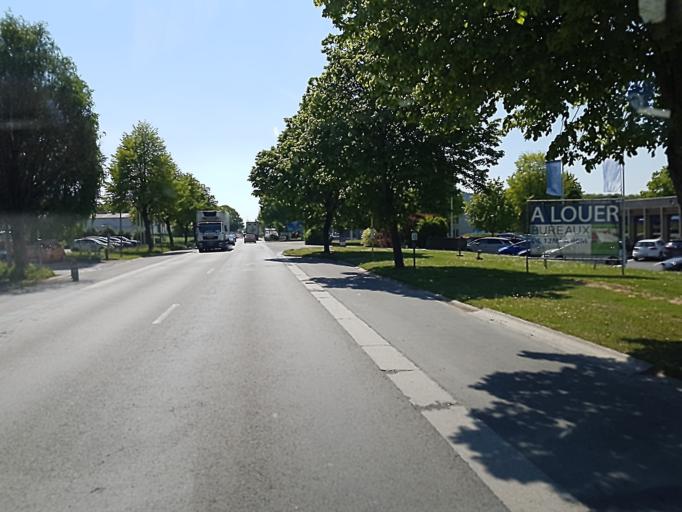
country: BE
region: Wallonia
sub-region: Province du Brabant Wallon
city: Nivelles
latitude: 50.5866
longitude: 4.3558
